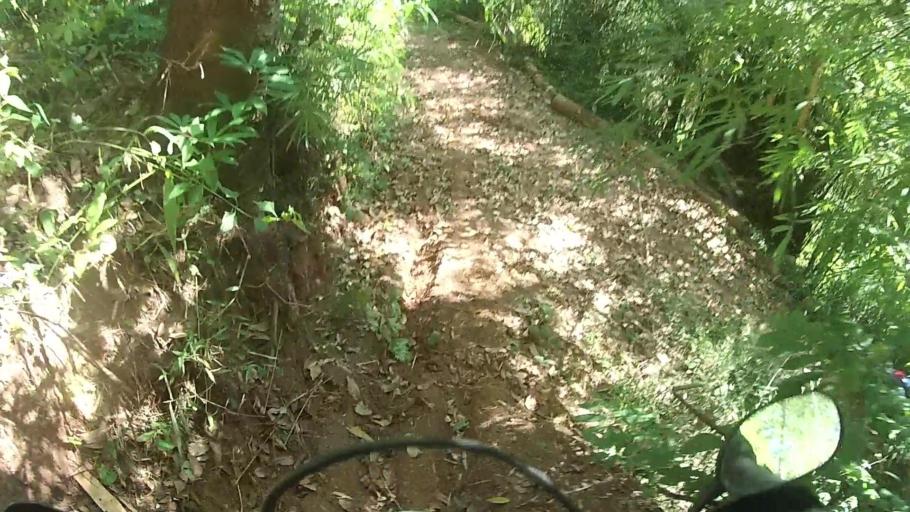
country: TH
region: Chiang Mai
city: Phrao
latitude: 19.3719
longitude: 99.3171
